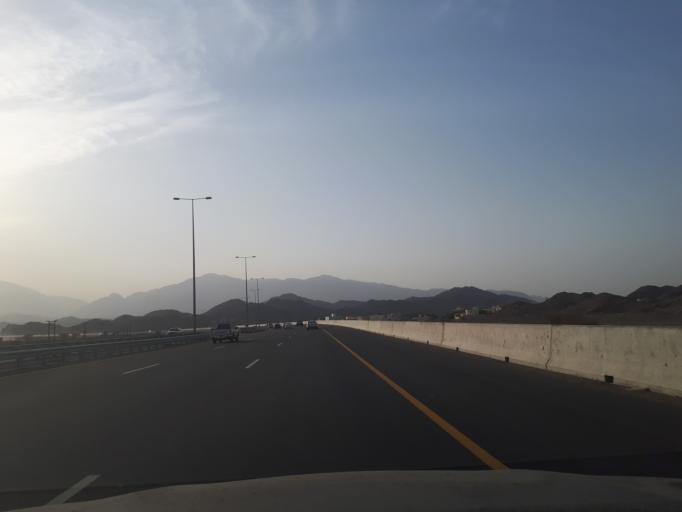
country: OM
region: Muhafazat ad Dakhiliyah
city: Bidbid
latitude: 23.3395
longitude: 58.1092
